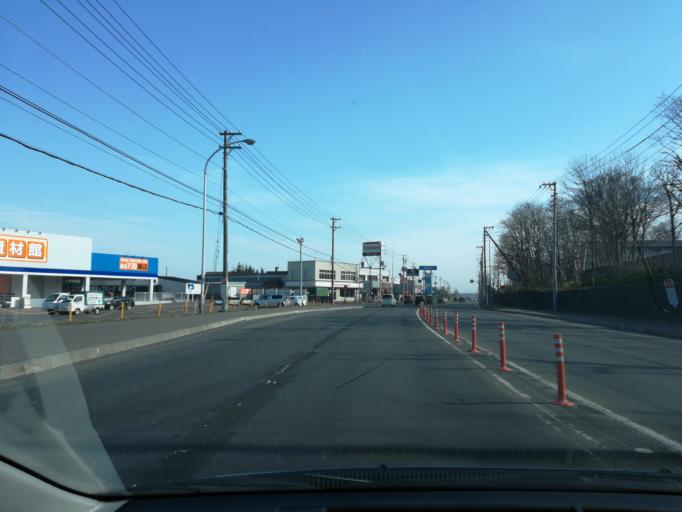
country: JP
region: Hokkaido
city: Iwamizawa
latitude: 43.2148
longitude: 141.7846
